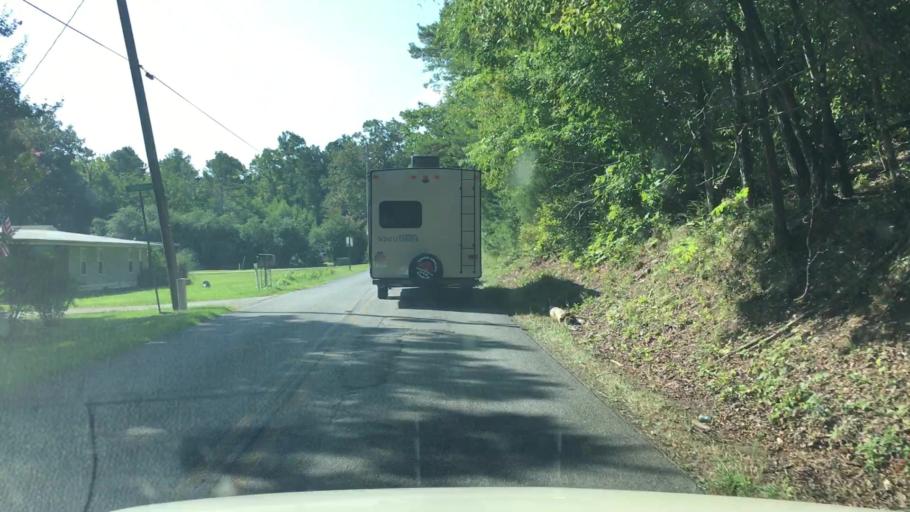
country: US
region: Arkansas
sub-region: Garland County
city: Piney
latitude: 34.5295
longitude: -93.3364
